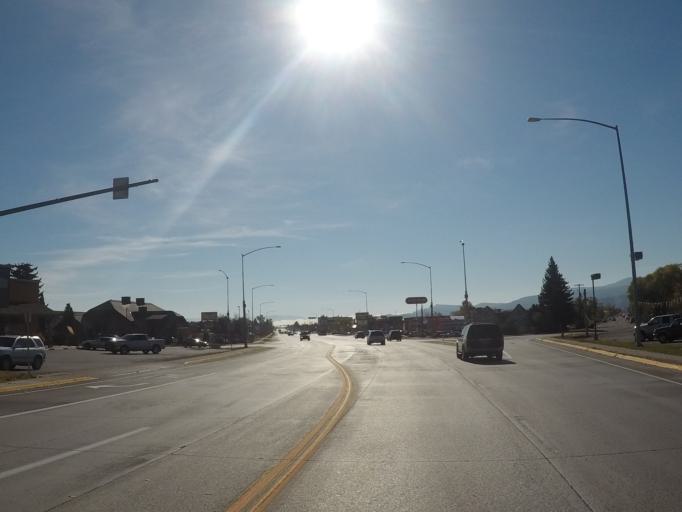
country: US
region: Montana
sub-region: Flathead County
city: Kalispell
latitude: 48.1869
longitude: -114.3095
